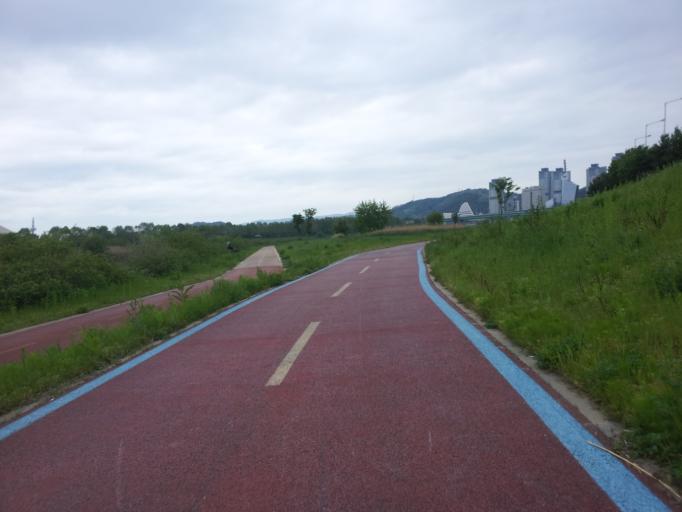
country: KR
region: Daejeon
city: Daejeon
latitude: 36.3638
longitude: 127.3982
